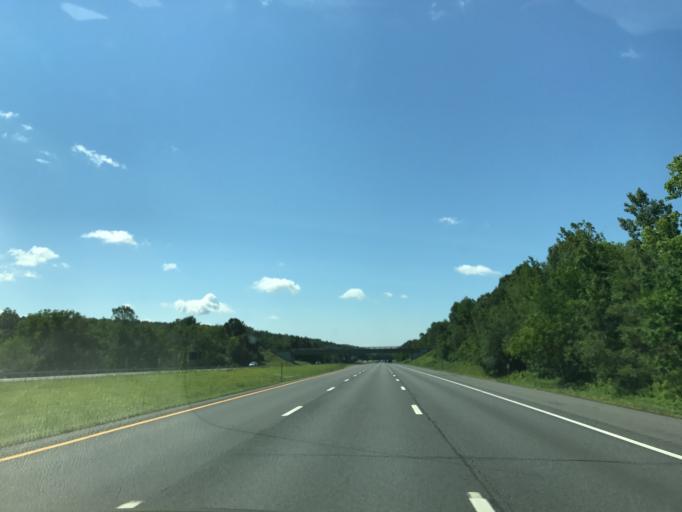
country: US
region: New York
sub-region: Rensselaer County
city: East Greenbush
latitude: 42.6035
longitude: -73.6833
